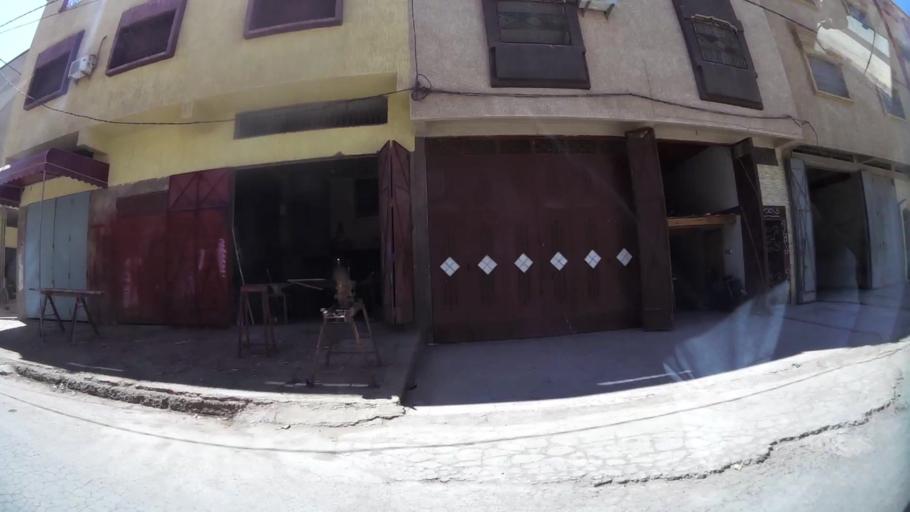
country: MA
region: Oriental
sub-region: Oujda-Angad
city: Oujda
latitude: 34.6886
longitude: -1.9391
